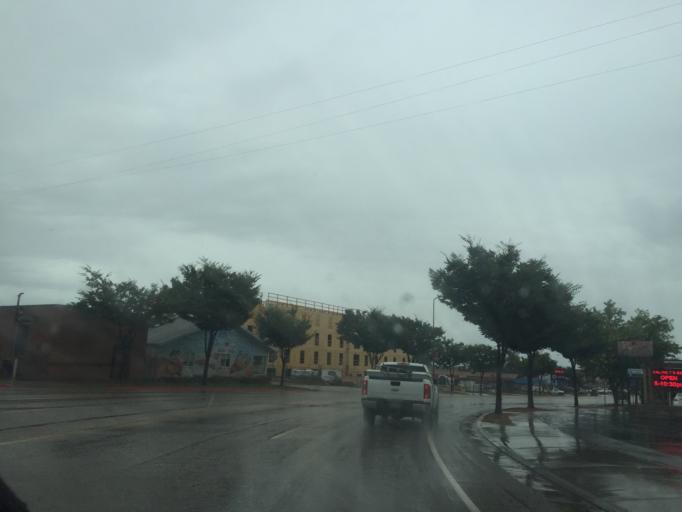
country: US
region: Utah
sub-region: Kane County
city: Kanab
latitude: 37.0478
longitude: -112.5267
